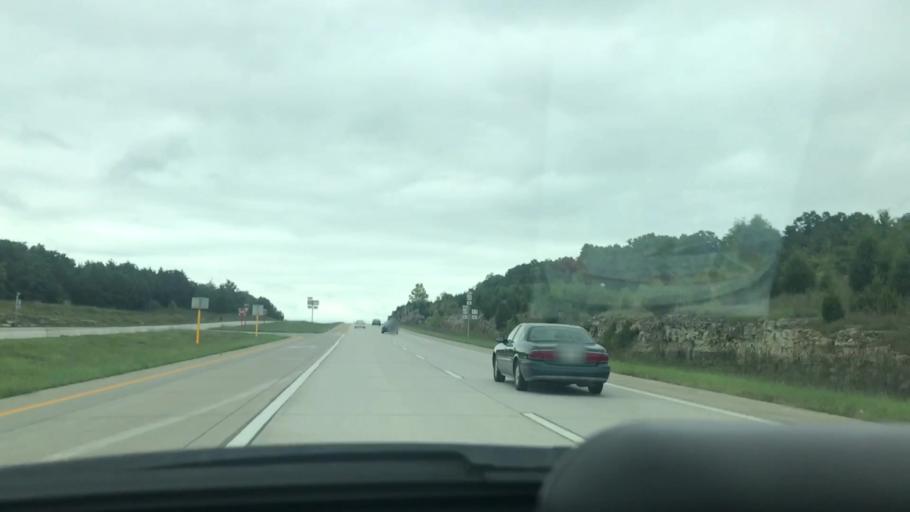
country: US
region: Missouri
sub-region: Dallas County
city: Buffalo
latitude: 37.5183
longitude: -93.1381
